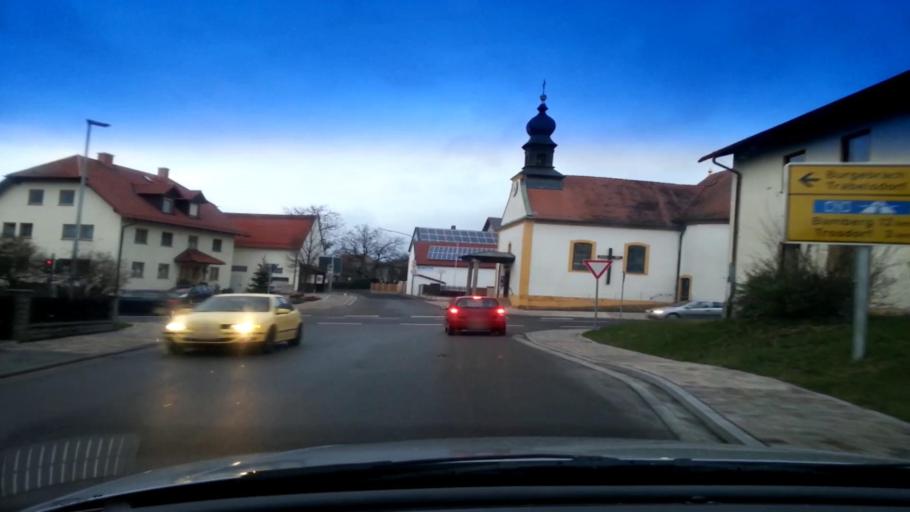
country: DE
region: Bavaria
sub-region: Upper Franconia
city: Viereth-Trunstadt
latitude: 49.9015
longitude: 10.7740
